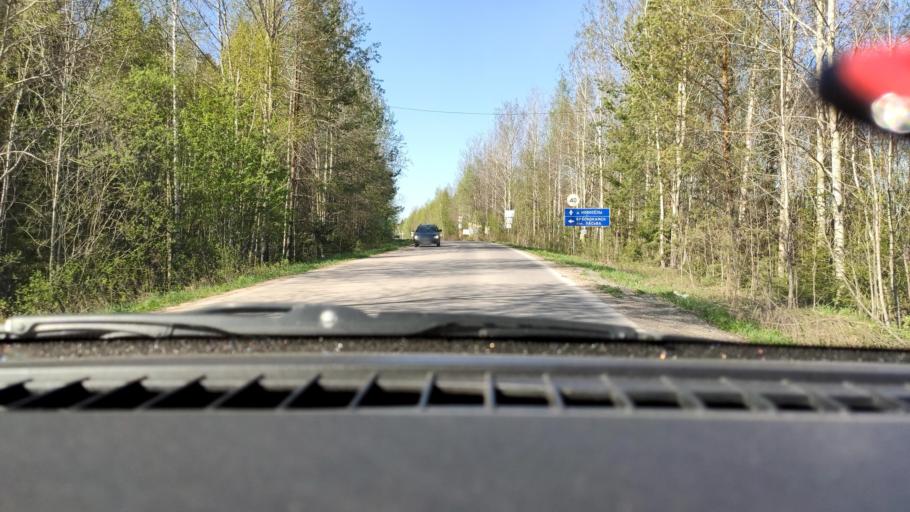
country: RU
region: Perm
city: Overyata
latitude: 58.0769
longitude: 56.0020
